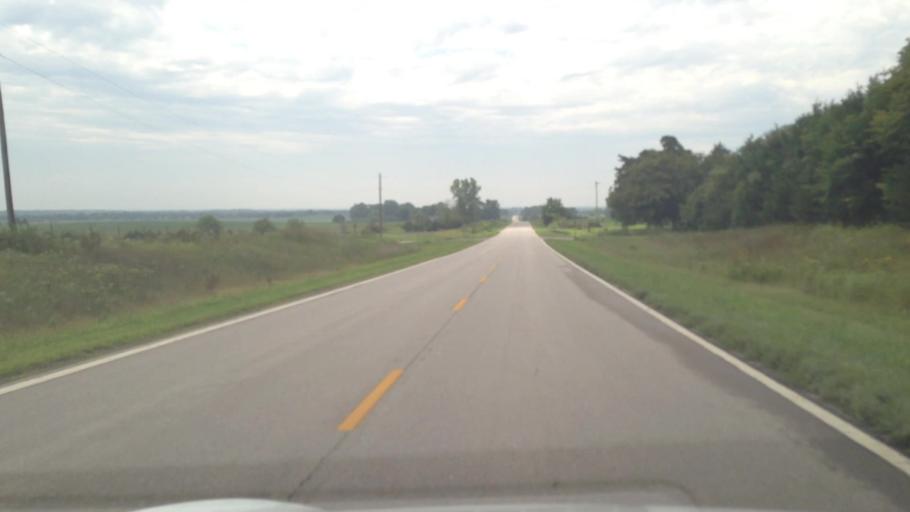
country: US
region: Kansas
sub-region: Bourbon County
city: Fort Scott
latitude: 37.8210
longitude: -94.9790
